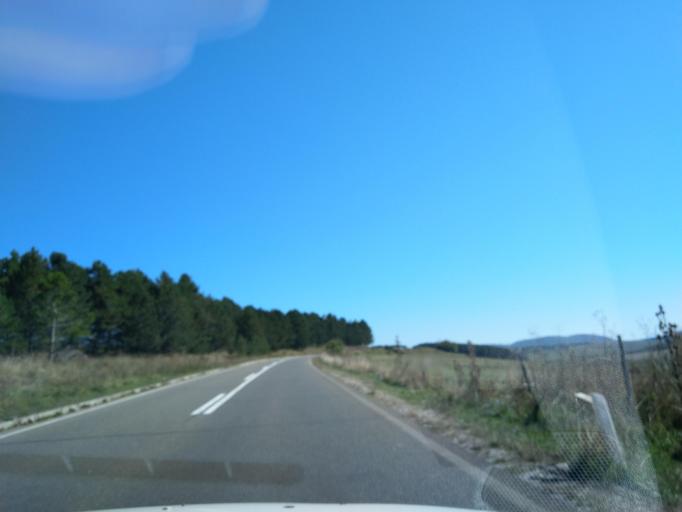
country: RS
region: Central Serbia
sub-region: Zlatiborski Okrug
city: Sjenica
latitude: 43.2677
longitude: 20.0342
